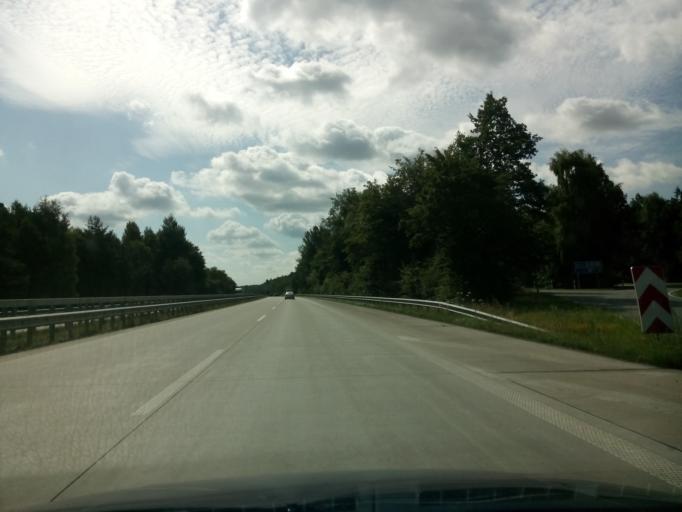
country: DE
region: Lower Saxony
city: Schwanewede
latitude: 53.2124
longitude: 8.6555
